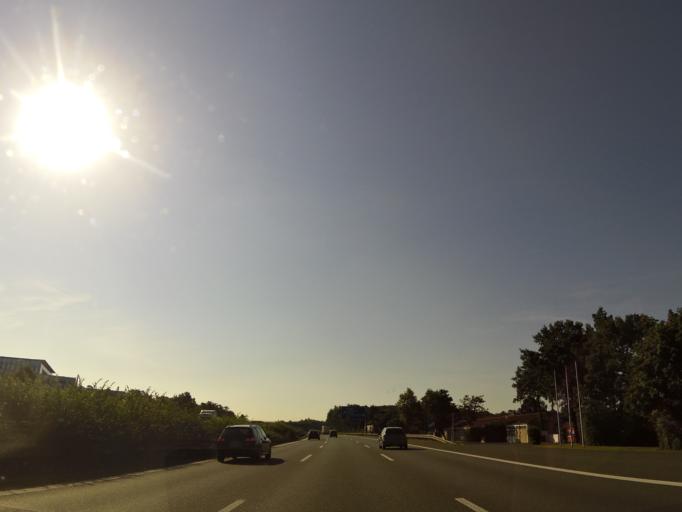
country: DE
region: Bavaria
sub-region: Regierungsbezirk Mittelfranken
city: Erlangen
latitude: 49.5414
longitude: 11.0217
